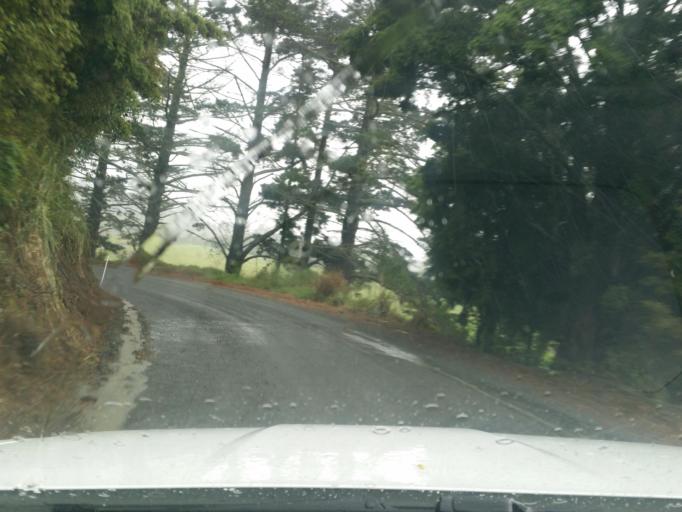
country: NZ
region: Northland
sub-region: Kaipara District
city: Dargaville
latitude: -35.8643
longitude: 174.0154
